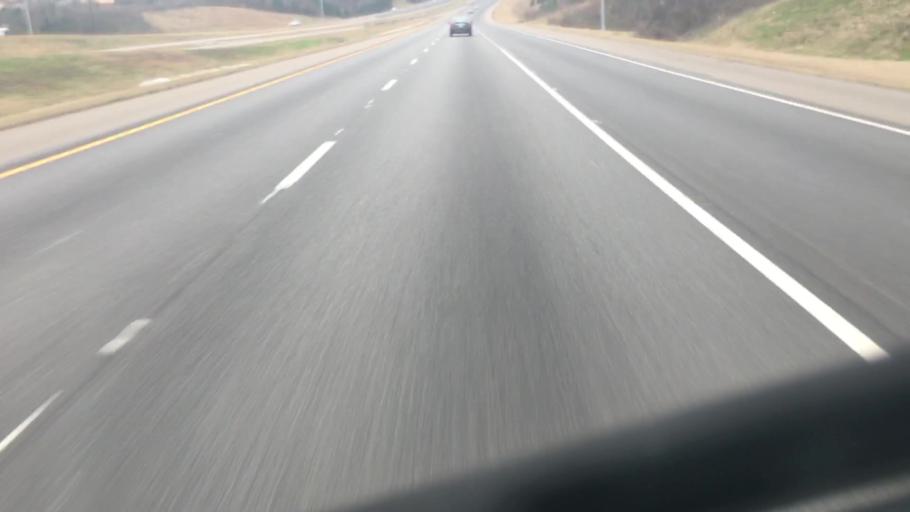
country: US
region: Alabama
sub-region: Jefferson County
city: Fultondale
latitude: 33.5764
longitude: -86.8194
